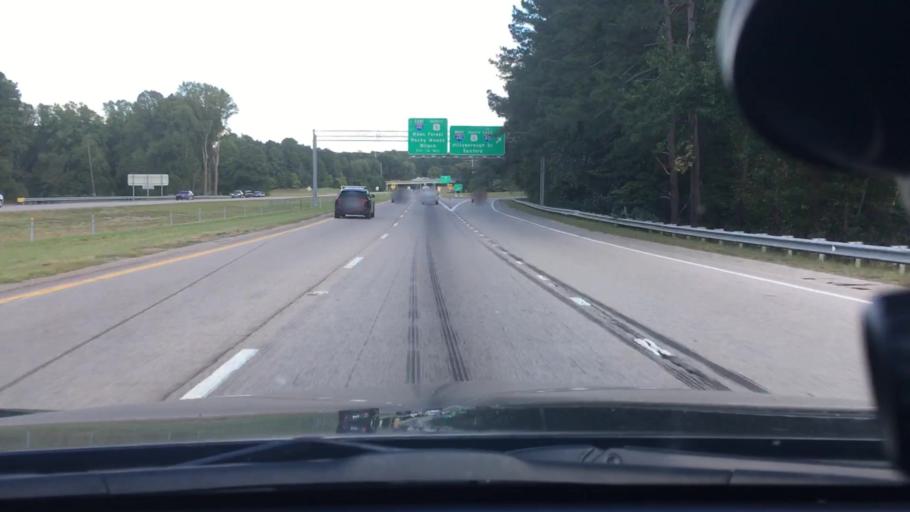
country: US
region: North Carolina
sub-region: Wake County
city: West Raleigh
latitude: 35.8037
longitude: -78.7001
